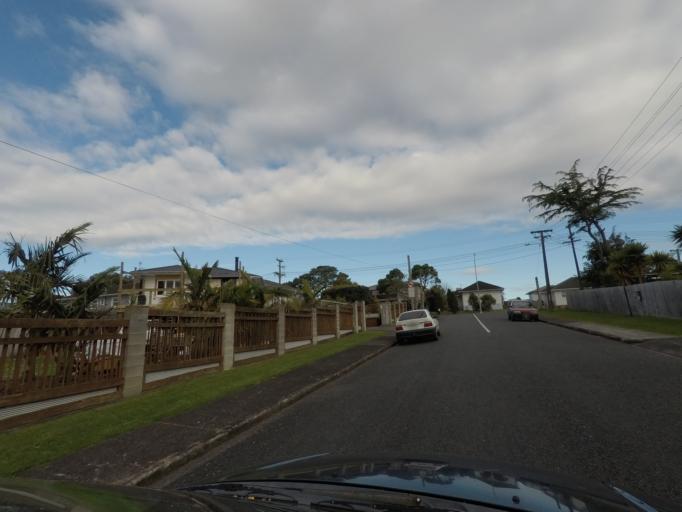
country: NZ
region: Auckland
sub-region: Auckland
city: Rosebank
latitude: -36.8856
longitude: 174.6551
